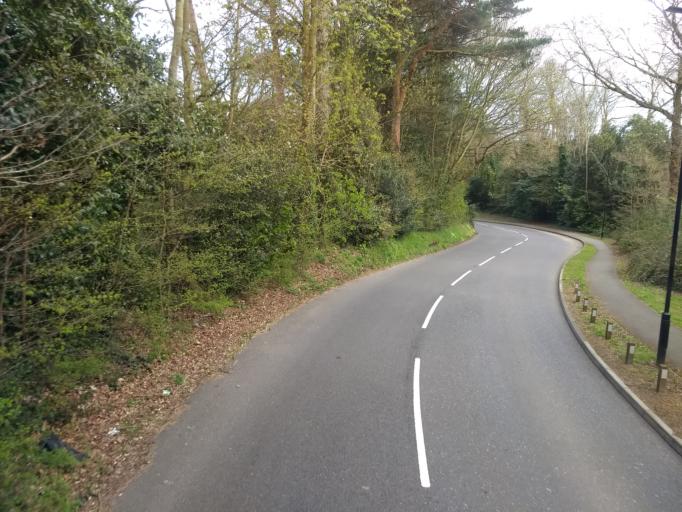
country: GB
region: England
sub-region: Isle of Wight
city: Seaview
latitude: 50.7175
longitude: -1.1268
